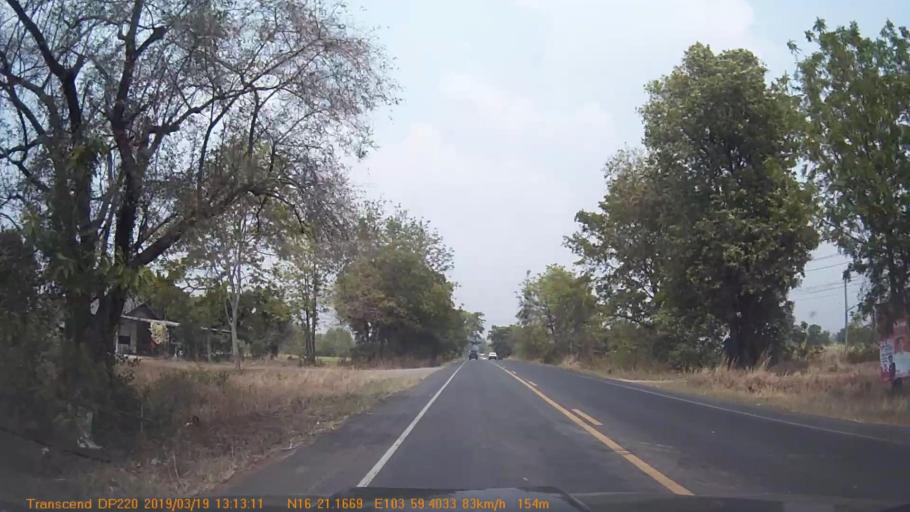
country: TH
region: Roi Et
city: Waeng
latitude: 16.3530
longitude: 103.9901
